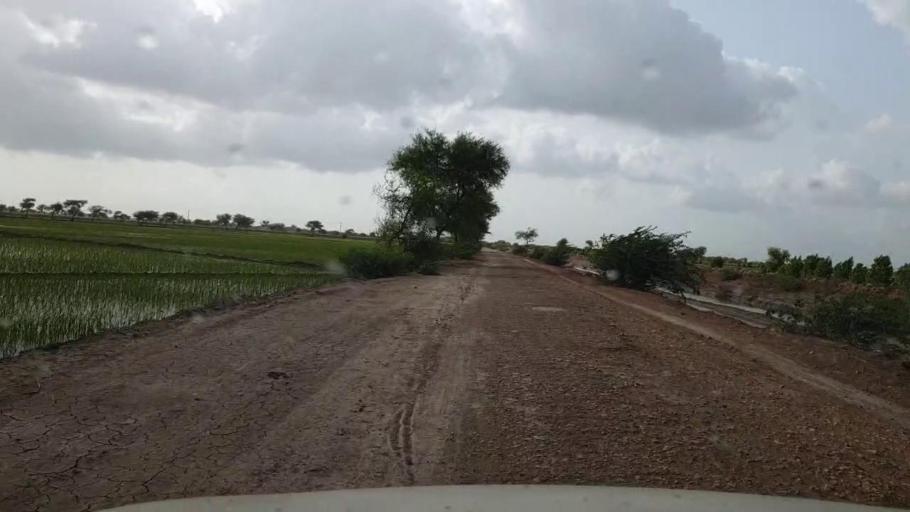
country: PK
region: Sindh
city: Kario
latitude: 24.7780
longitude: 68.5903
